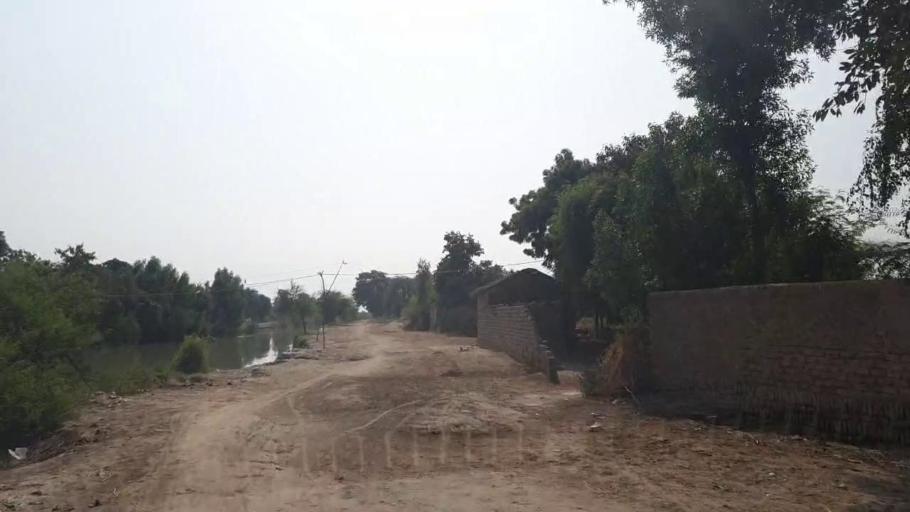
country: PK
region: Sindh
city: Badin
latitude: 24.6509
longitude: 68.8447
